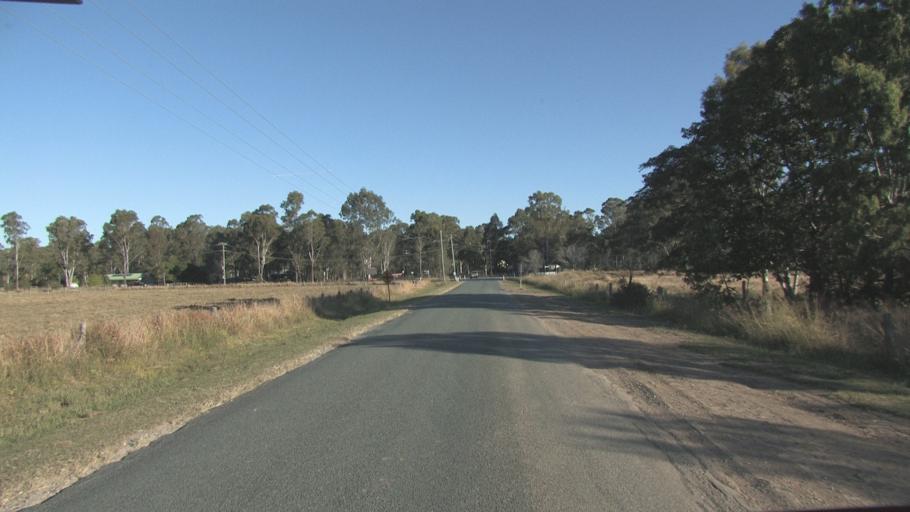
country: AU
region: Queensland
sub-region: Logan
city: Chambers Flat
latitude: -27.7821
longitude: 153.1352
